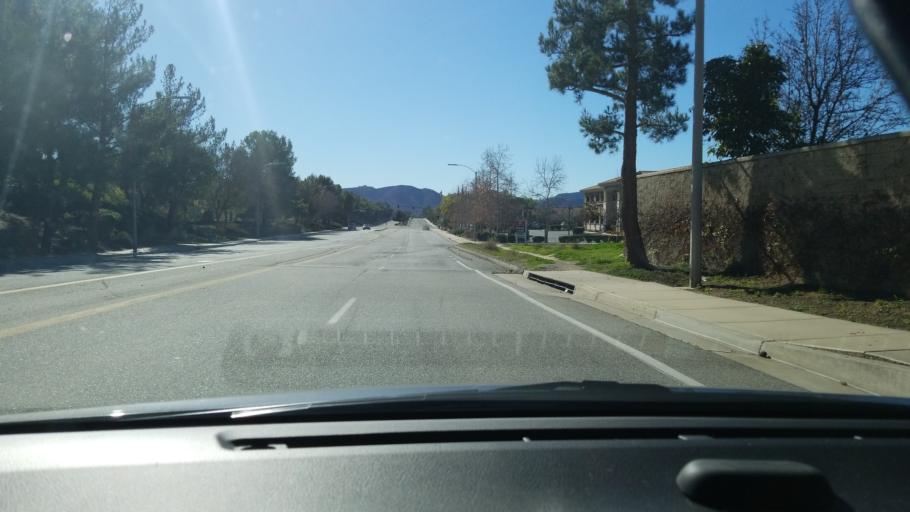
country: US
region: California
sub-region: Riverside County
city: Murrieta Hot Springs
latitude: 33.5467
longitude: -117.1529
